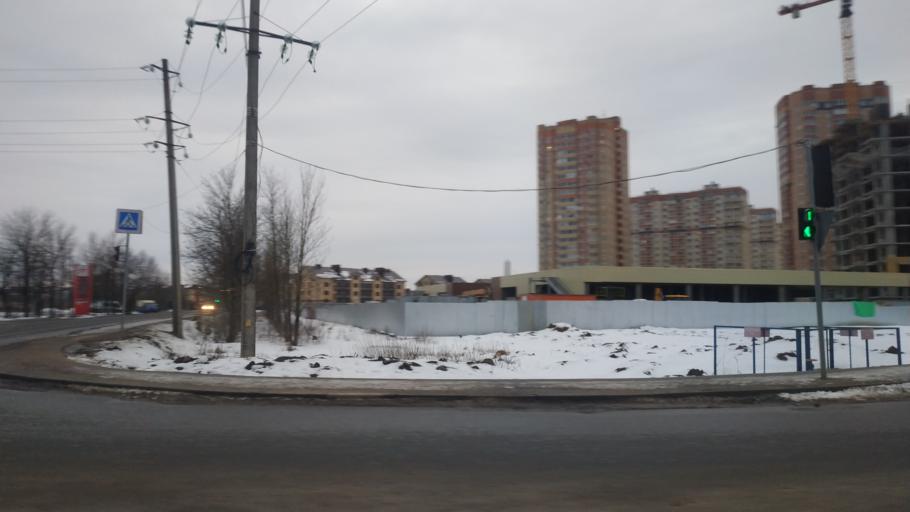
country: RU
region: Tverskaya
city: Tver
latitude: 56.8215
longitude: 35.8760
